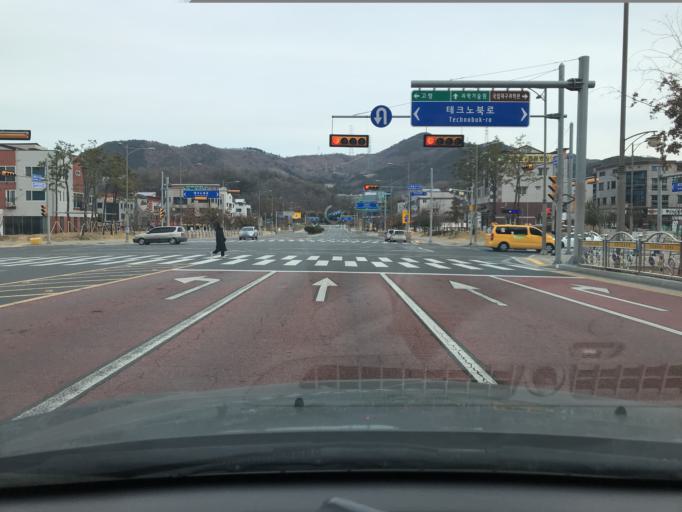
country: KR
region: Daegu
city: Hwawon
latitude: 35.6964
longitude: 128.4579
